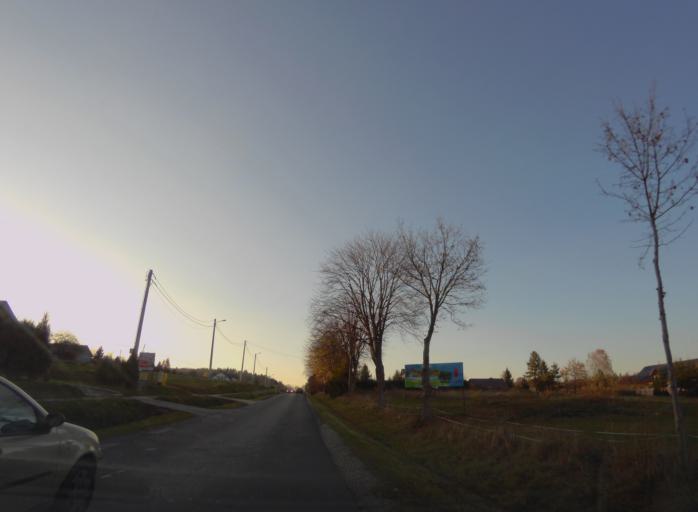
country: PL
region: Subcarpathian Voivodeship
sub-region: Powiat leski
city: Polanczyk
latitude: 49.3906
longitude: 22.3919
